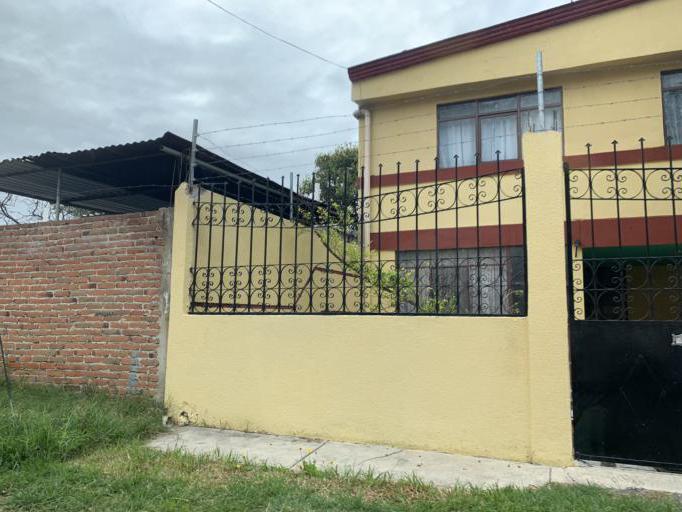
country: MX
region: Puebla
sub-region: Puebla
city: Articulo Primero Constitucional
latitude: 18.9856
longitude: -98.1938
